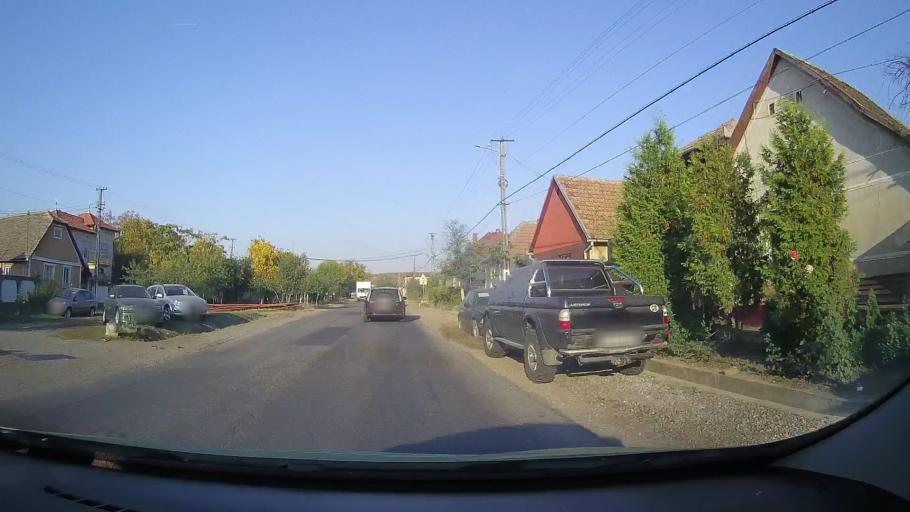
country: RO
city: Masca
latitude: 46.2944
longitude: 21.6678
